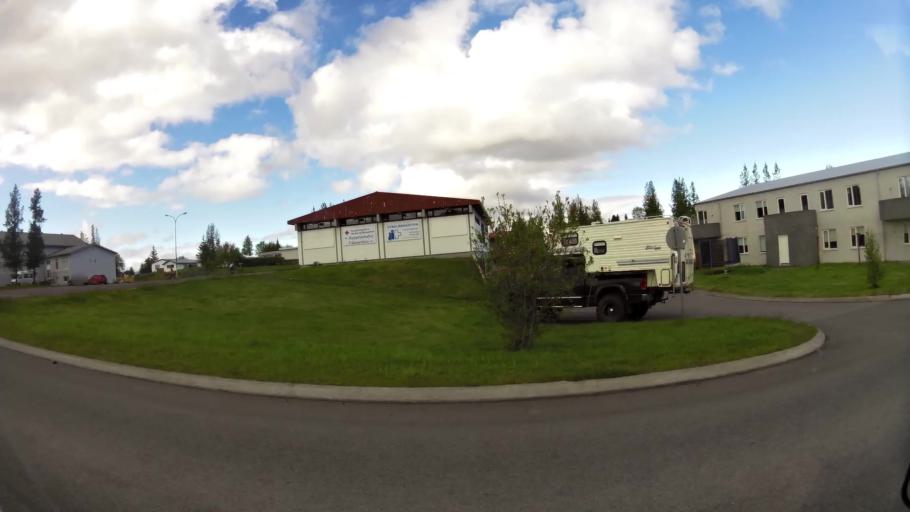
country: IS
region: East
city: Egilsstadir
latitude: 65.2623
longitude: -14.3925
